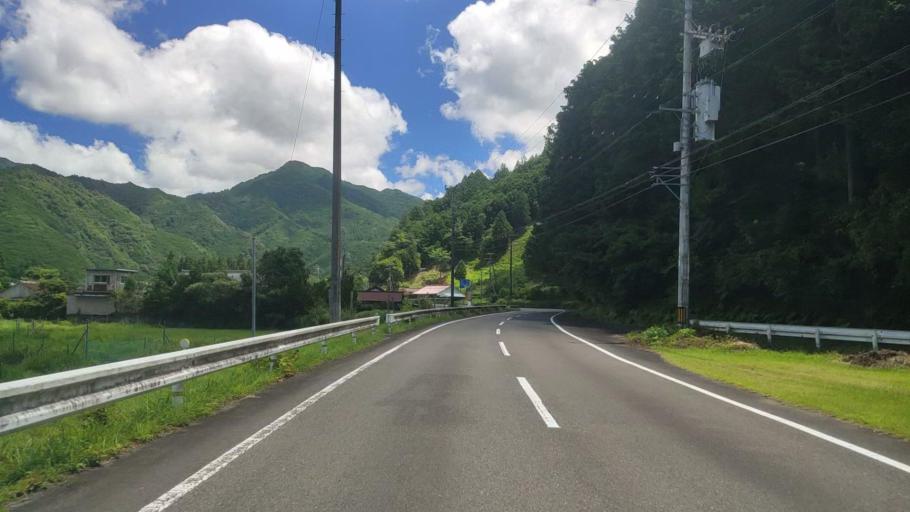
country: JP
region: Mie
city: Owase
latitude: 33.9821
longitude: 136.0372
